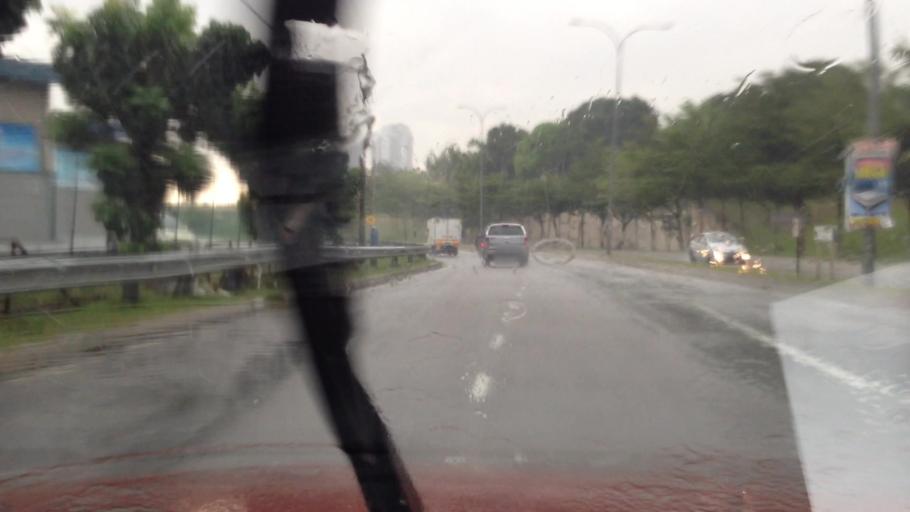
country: MY
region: Selangor
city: Subang Jaya
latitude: 3.0255
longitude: 101.5886
